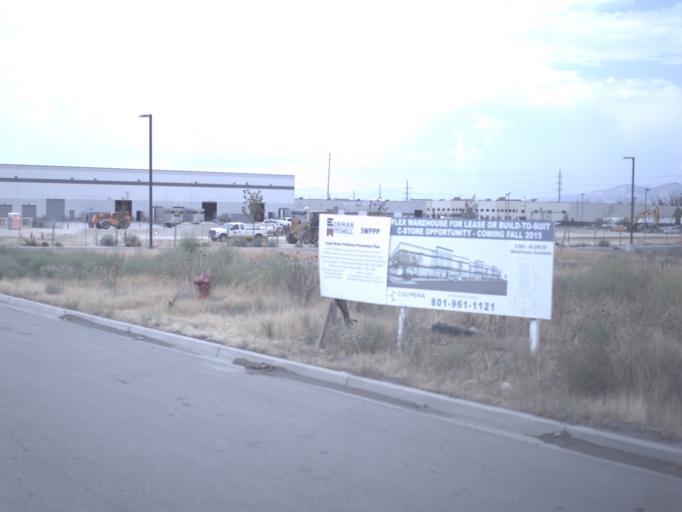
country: US
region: Utah
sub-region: Utah County
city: Lindon
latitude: 40.3263
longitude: -111.7384
